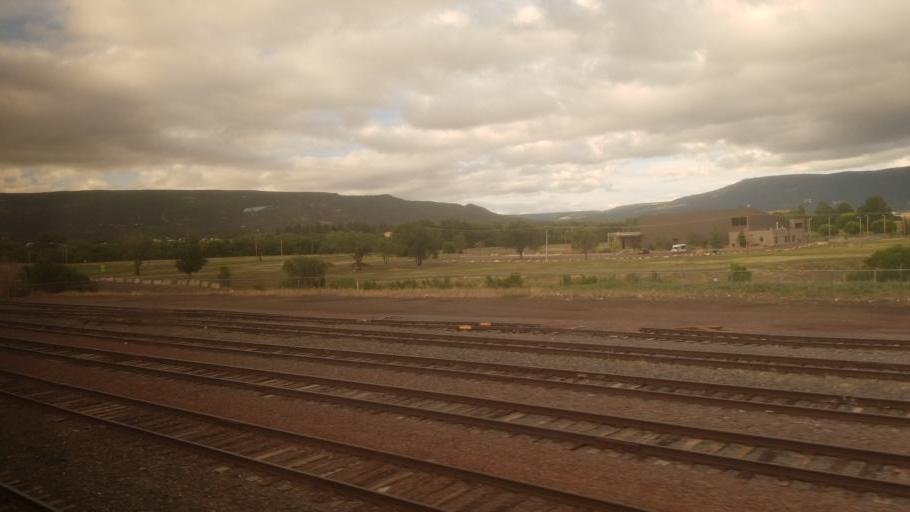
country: US
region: New Mexico
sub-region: Colfax County
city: Raton
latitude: 36.8982
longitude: -104.4381
